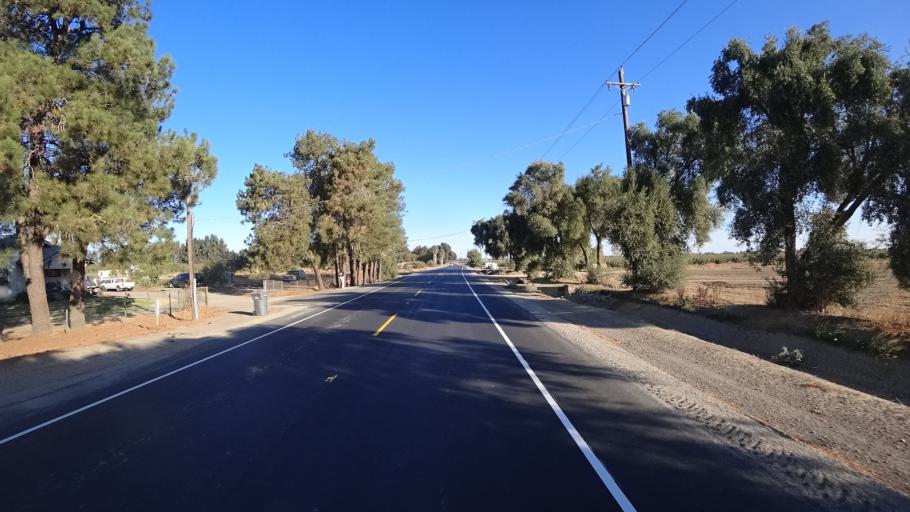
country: US
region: California
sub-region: Yolo County
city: Woodland
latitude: 38.6334
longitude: -121.7848
